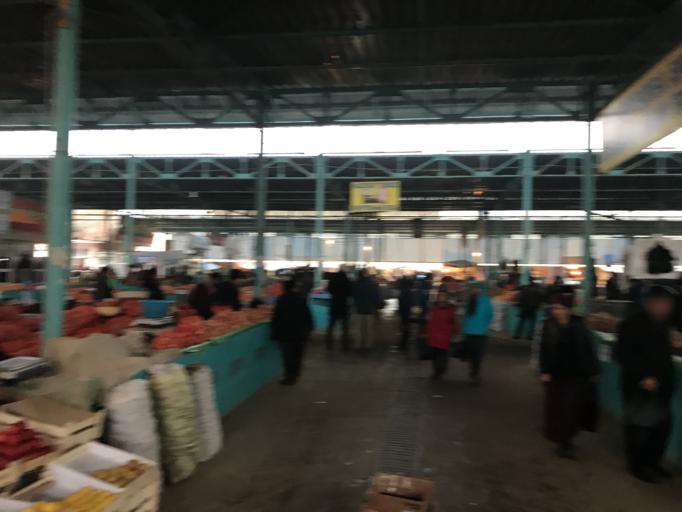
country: UZ
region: Toshkent
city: Yangiyul
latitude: 41.1175
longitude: 69.0541
